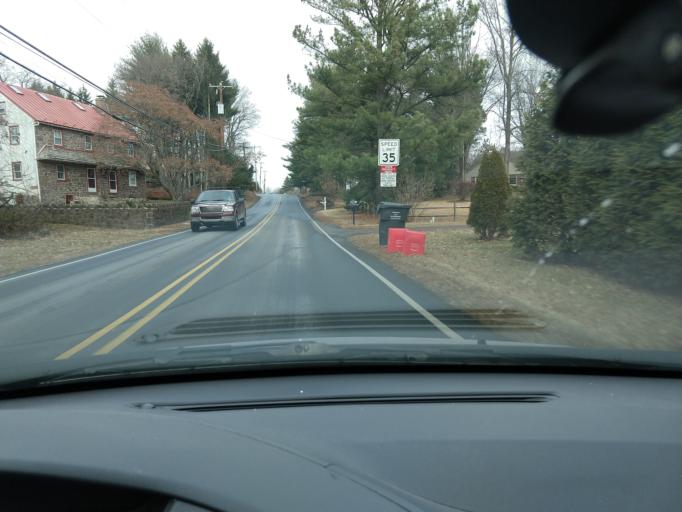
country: US
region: Pennsylvania
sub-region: Chester County
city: South Pottstown
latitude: 40.2096
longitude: -75.6651
